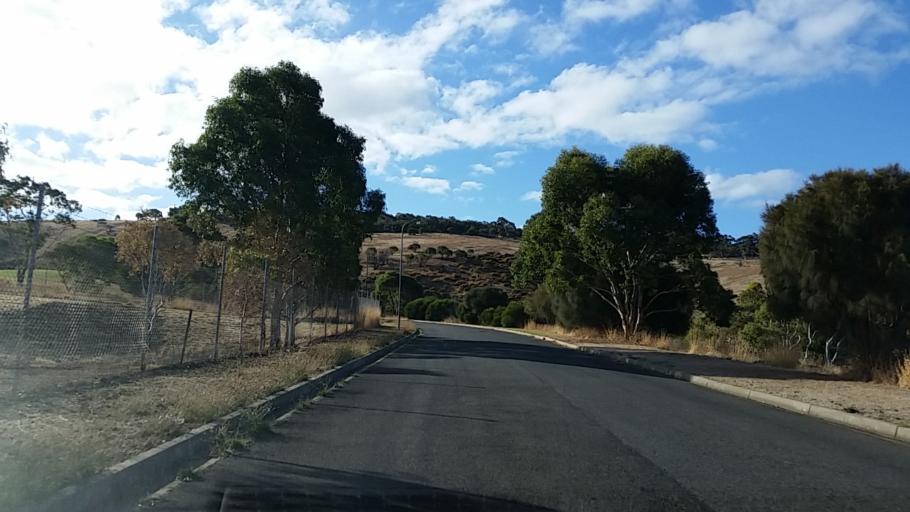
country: AU
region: South Australia
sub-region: Yankalilla
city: Normanville
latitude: -35.5013
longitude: 138.2555
